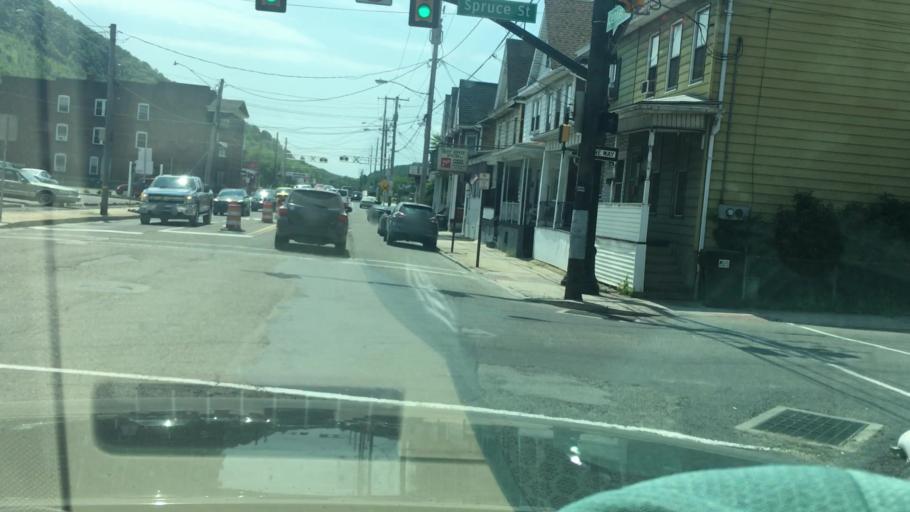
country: US
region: Pennsylvania
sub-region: Schuylkill County
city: Tamaqua
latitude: 40.7952
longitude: -75.9685
